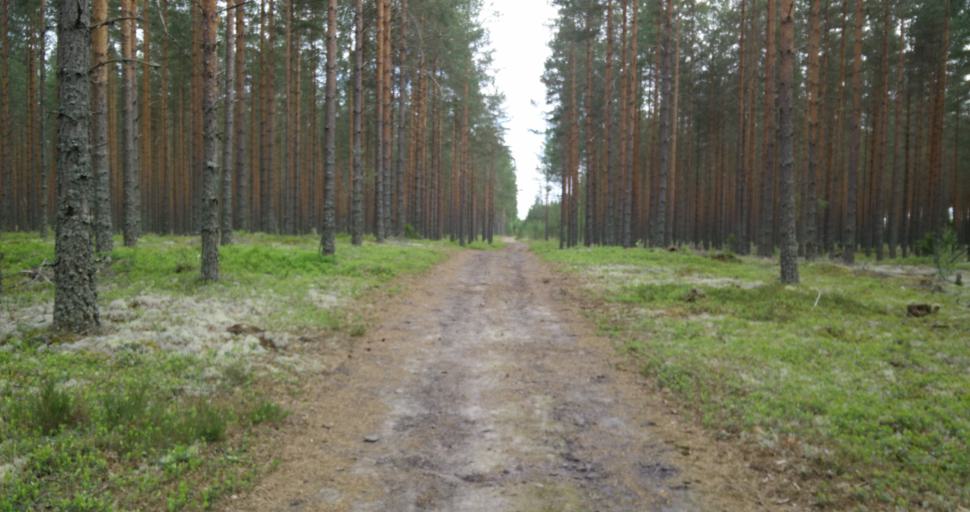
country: SE
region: Vaermland
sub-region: Hagfors Kommun
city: Hagfors
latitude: 60.0158
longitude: 13.5861
